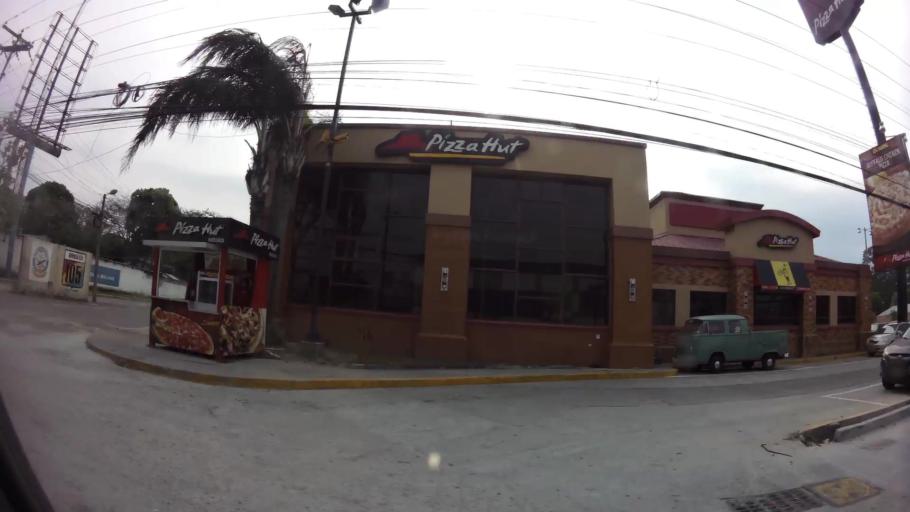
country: HN
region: Cortes
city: San Pedro Sula
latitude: 15.5198
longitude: -88.0254
